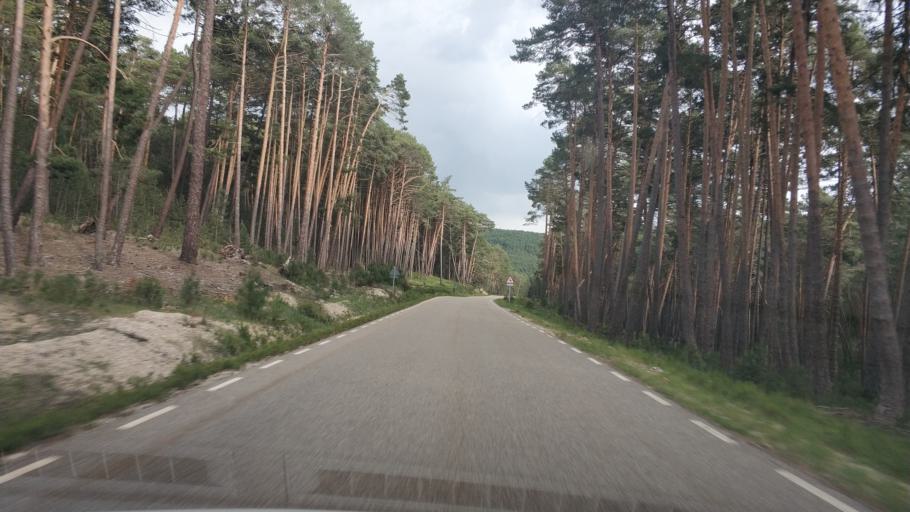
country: ES
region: Castille and Leon
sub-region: Provincia de Soria
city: San Leonardo de Yague
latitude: 41.8586
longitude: -3.0774
